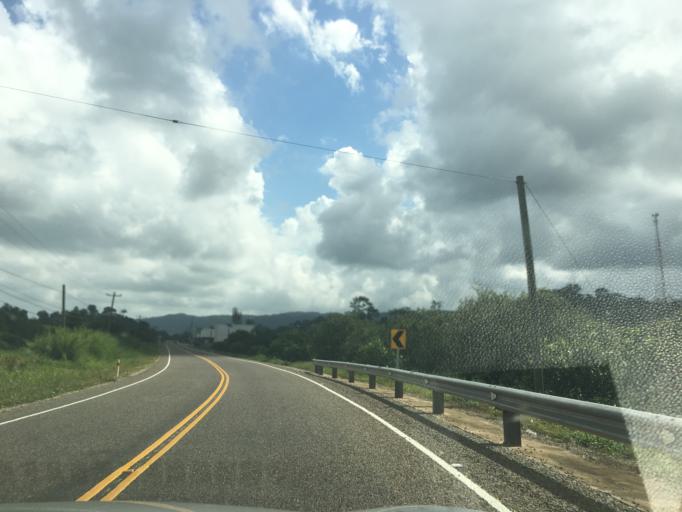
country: BZ
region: Stann Creek
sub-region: Dangriga
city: Dangriga
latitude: 16.9929
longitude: -88.4066
